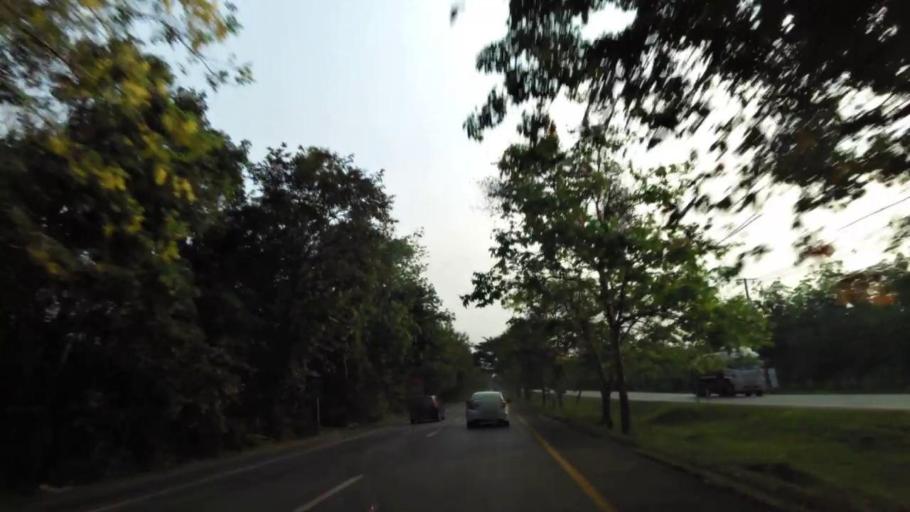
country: TH
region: Chanthaburi
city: Chanthaburi
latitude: 12.5367
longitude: 102.1576
